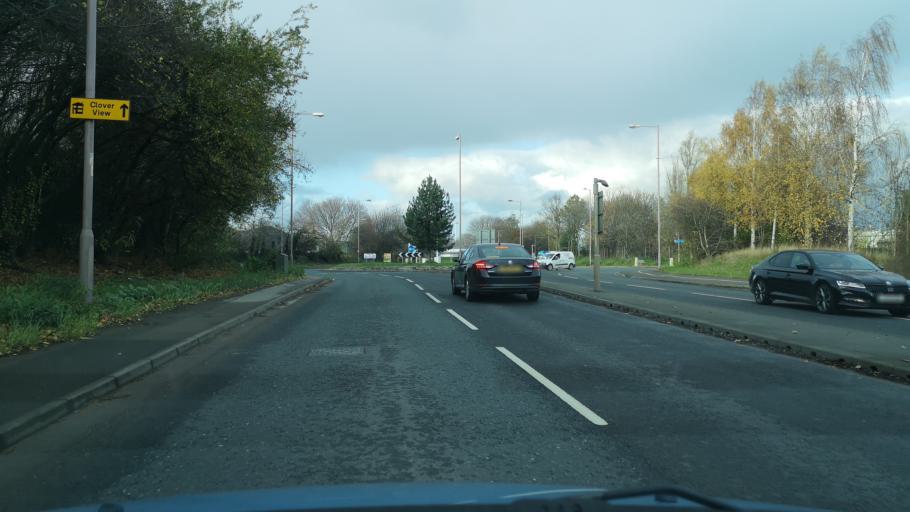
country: GB
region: England
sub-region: City and Borough of Wakefield
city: Normanton
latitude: 53.7039
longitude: -1.3964
